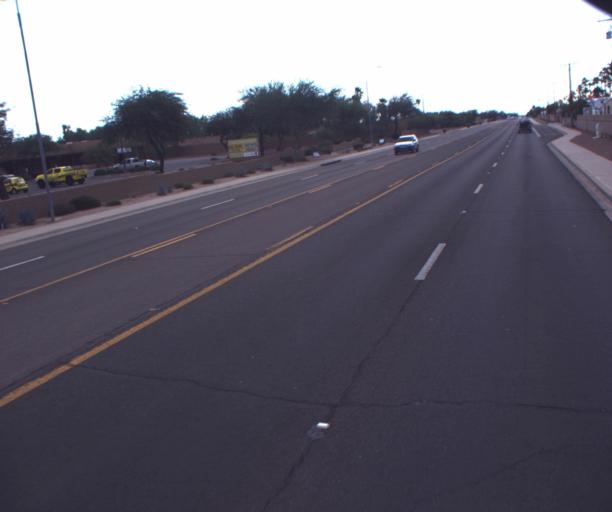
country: US
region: Arizona
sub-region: Pinal County
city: Apache Junction
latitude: 33.4062
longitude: -111.5462
